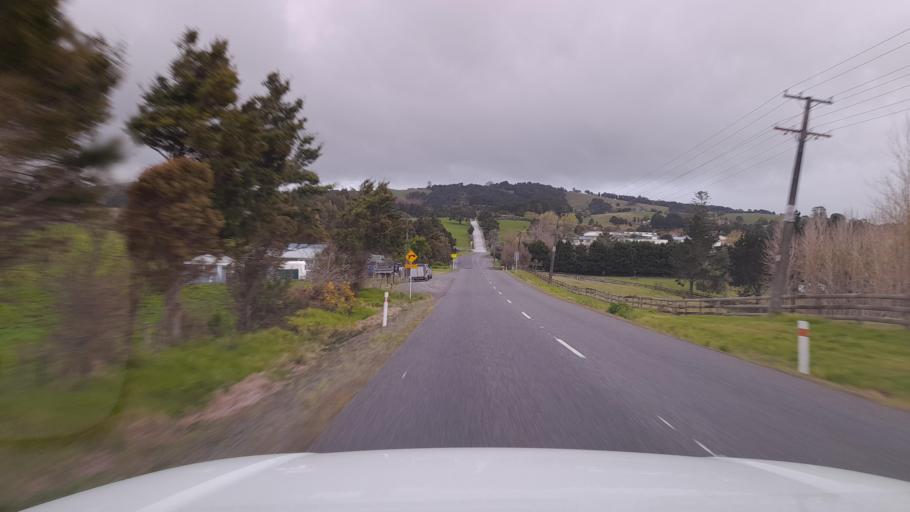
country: NZ
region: Northland
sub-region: Whangarei
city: Maungatapere
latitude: -35.6601
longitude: 174.2245
